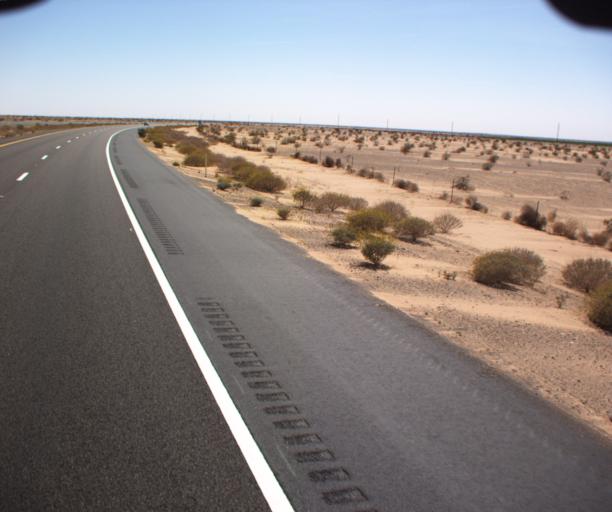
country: US
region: Arizona
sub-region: Yuma County
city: Somerton
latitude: 32.5053
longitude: -114.5584
